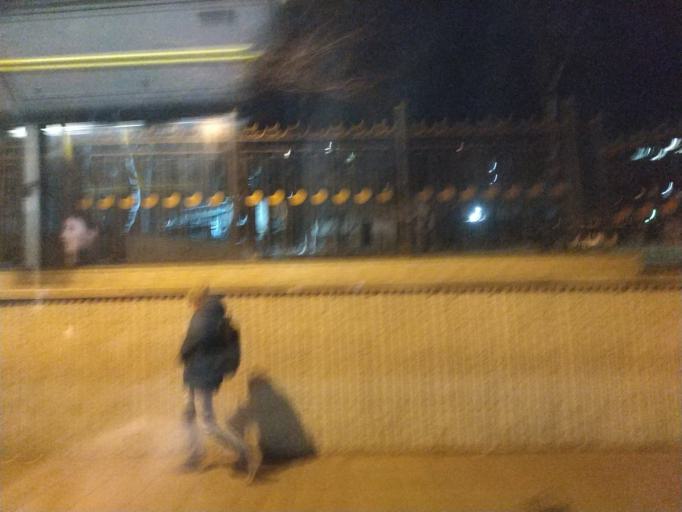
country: RU
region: Primorskiy
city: Vladivostok
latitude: 43.1228
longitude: 131.8881
